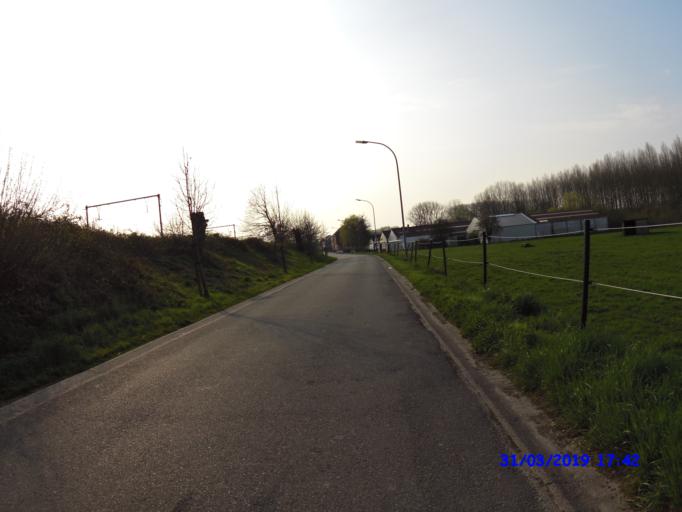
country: BE
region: Flanders
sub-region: Provincie Vlaams-Brabant
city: Liedekerke
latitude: 50.8825
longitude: 4.1228
